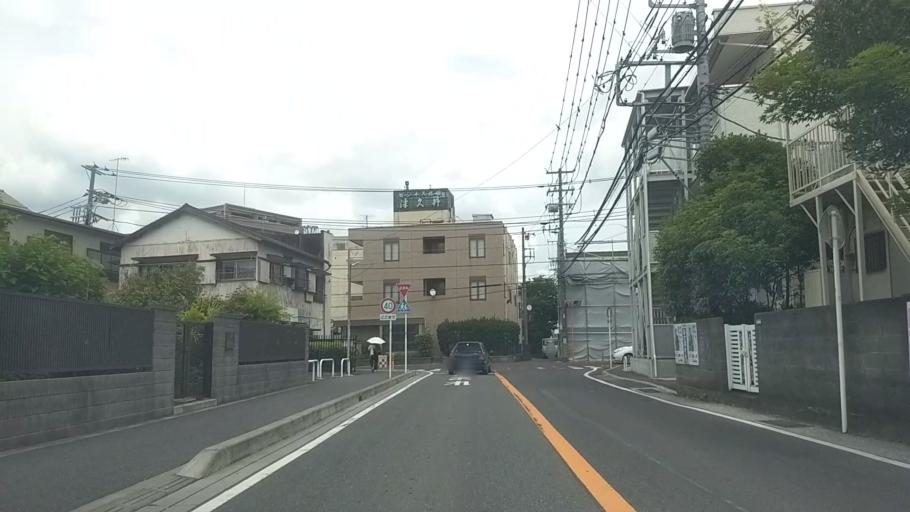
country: JP
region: Kanagawa
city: Kamakura
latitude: 35.3483
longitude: 139.5289
